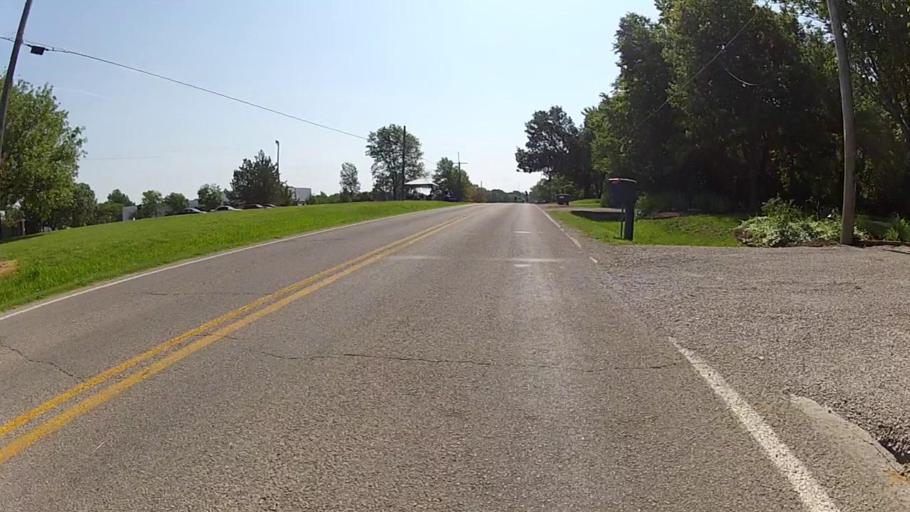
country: US
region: Kansas
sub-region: Montgomery County
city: Independence
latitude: 37.1929
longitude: -95.7224
